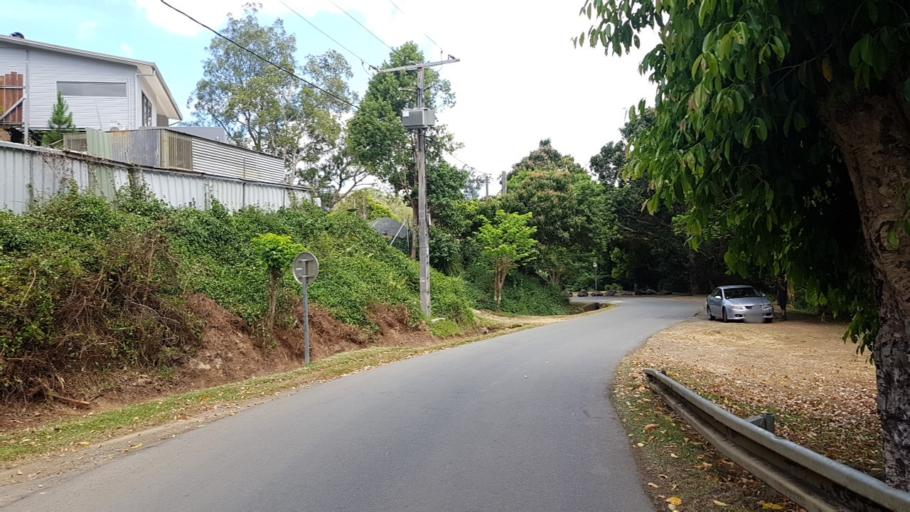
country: NC
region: South Province
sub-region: Dumbea
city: Dumbea
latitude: -22.1780
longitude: 166.4814
